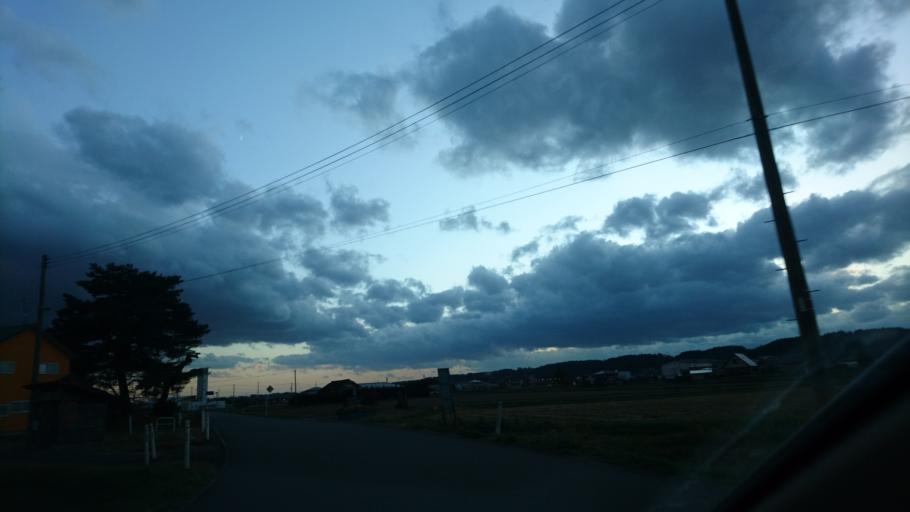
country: JP
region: Iwate
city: Mizusawa
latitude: 39.0645
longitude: 141.1396
